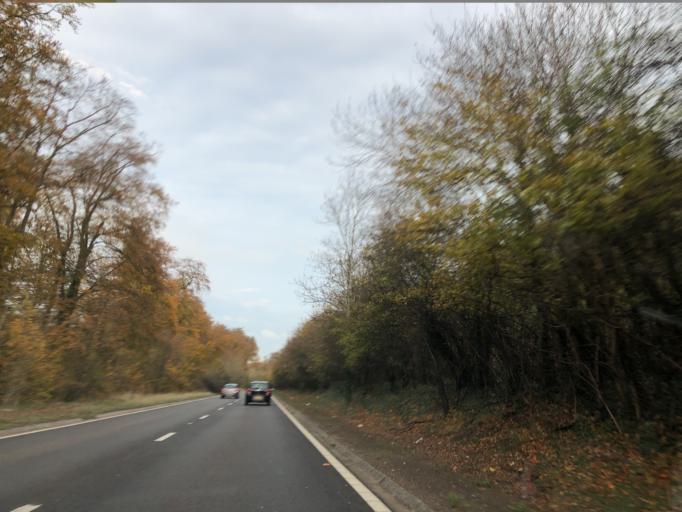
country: GB
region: England
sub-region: Royal Borough of Windsor and Maidenhead
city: Bisham
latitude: 51.5474
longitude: -0.7825
